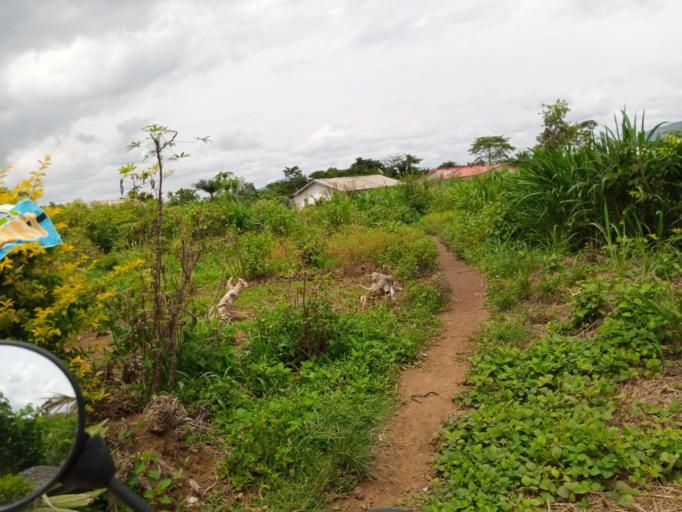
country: SL
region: Southern Province
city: Moyamba
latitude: 8.1620
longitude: -12.4229
